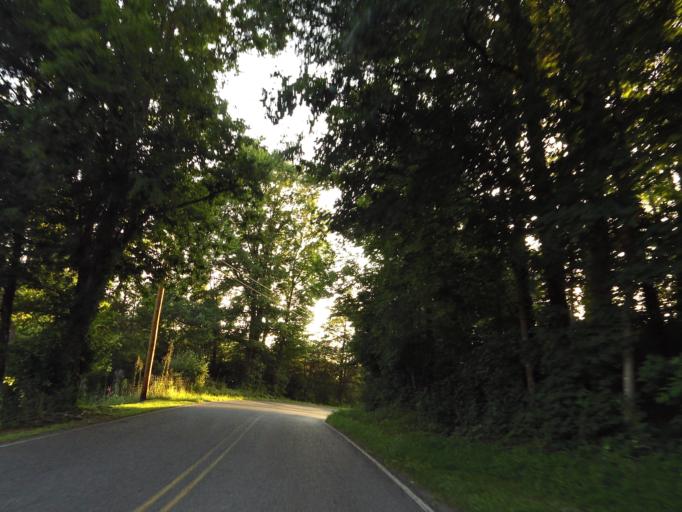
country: US
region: Tennessee
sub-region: Blount County
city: Maryville
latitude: 35.6562
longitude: -83.9587
